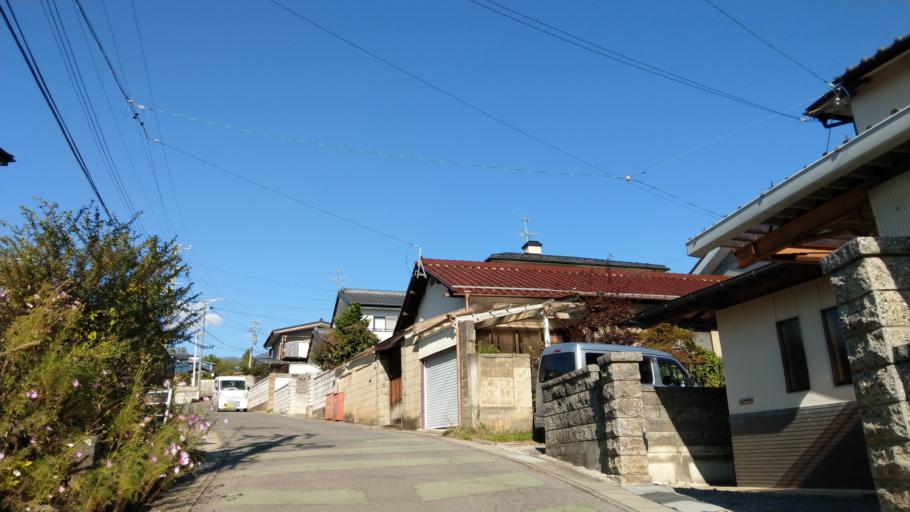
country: JP
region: Nagano
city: Komoro
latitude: 36.3340
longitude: 138.4295
